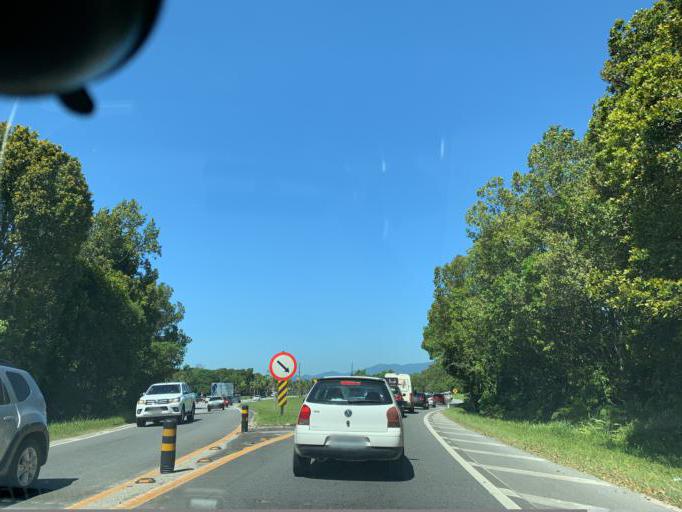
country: BR
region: Sao Paulo
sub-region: Bertioga
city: Bertioga
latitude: -23.7870
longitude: -46.0264
